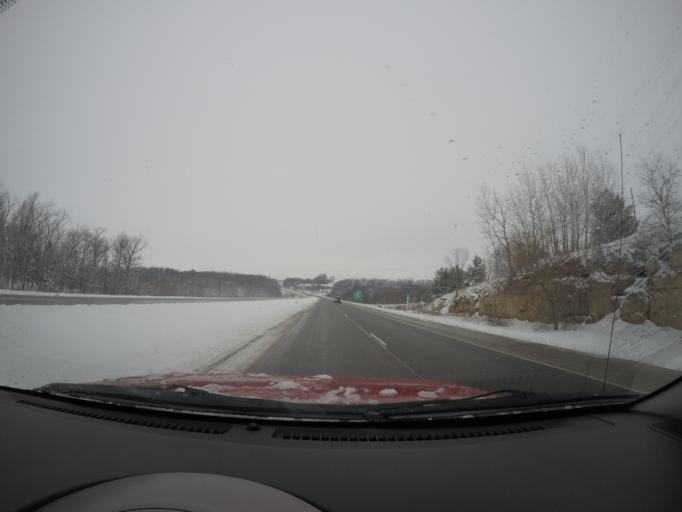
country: US
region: Minnesota
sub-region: Winona County
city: Lewiston
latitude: 43.9309
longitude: -91.8709
